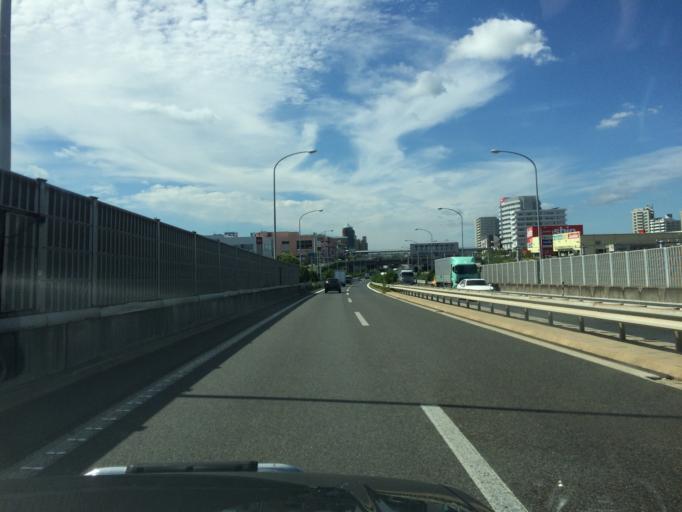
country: JP
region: Osaka
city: Izumi
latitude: 34.4639
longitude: 135.4613
